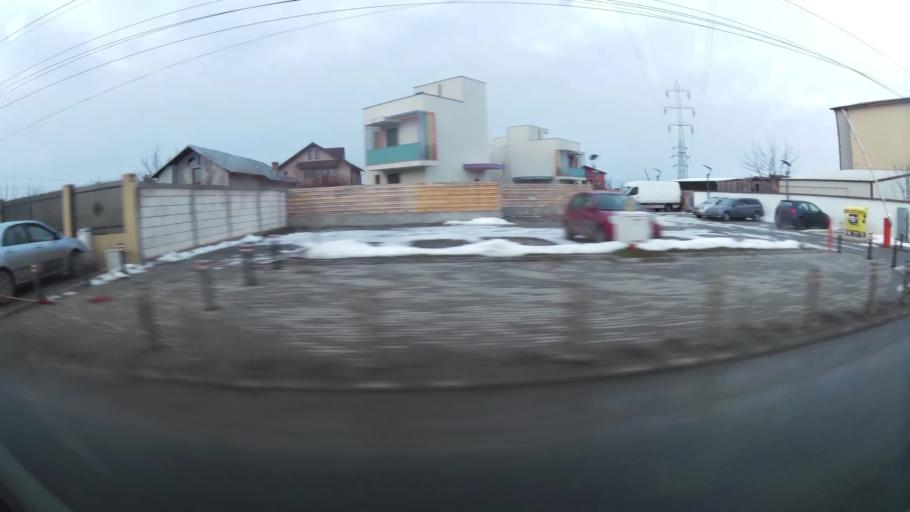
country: RO
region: Ilfov
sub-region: Comuna Popesti-Leordeni
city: Popesti-Leordeni
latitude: 44.3804
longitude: 26.1843
